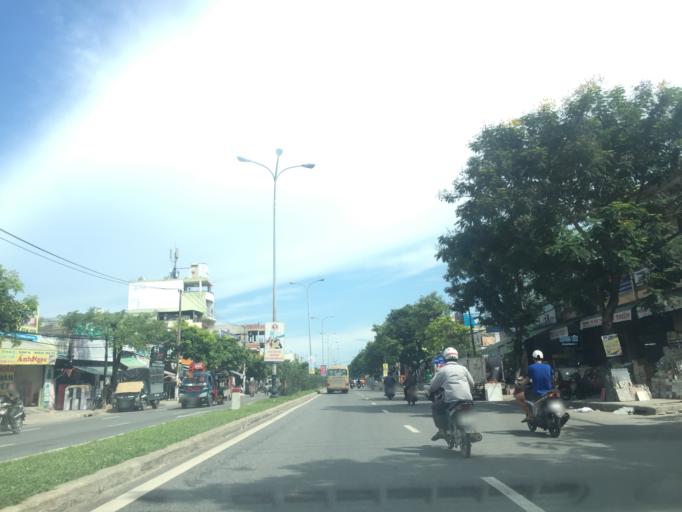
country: VN
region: Da Nang
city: Lien Chieu
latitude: 16.0650
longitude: 108.1558
